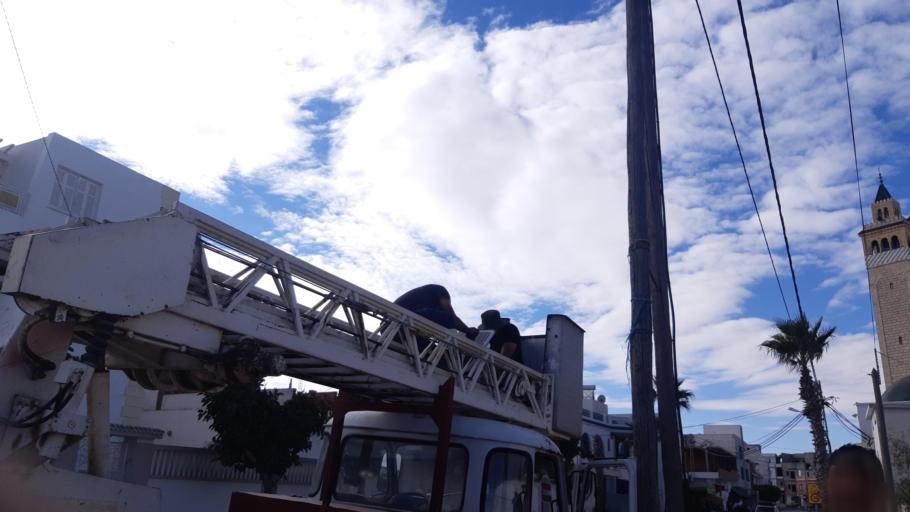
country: TN
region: Susah
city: Akouda
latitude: 35.8673
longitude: 10.5459
